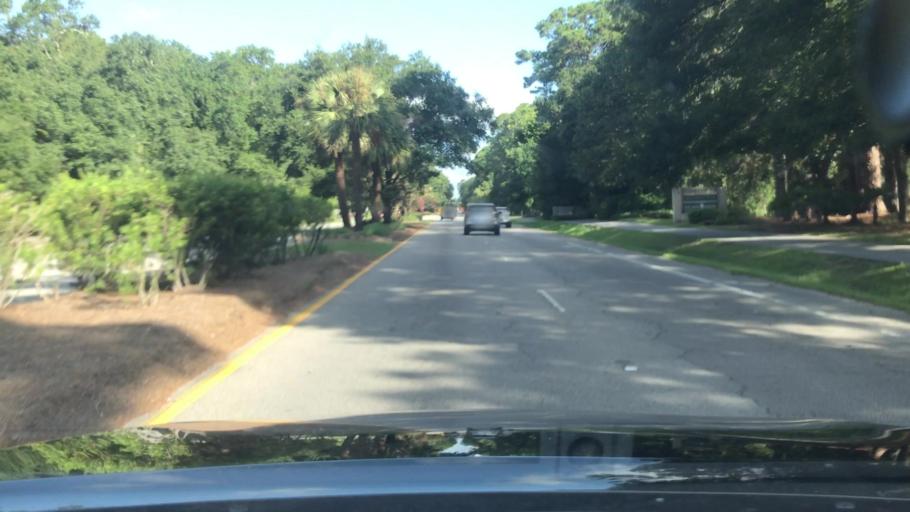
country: US
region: South Carolina
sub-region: Beaufort County
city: Hilton Head Island
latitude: 32.1489
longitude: -80.7571
